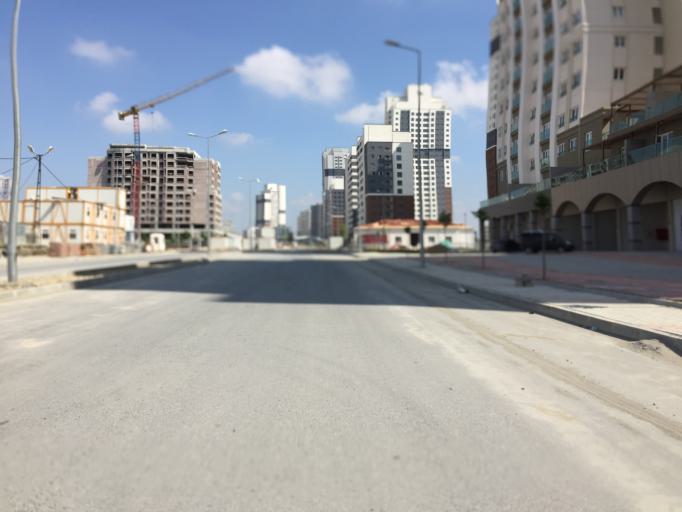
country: TR
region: Istanbul
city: Esenyurt
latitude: 41.0880
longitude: 28.6546
